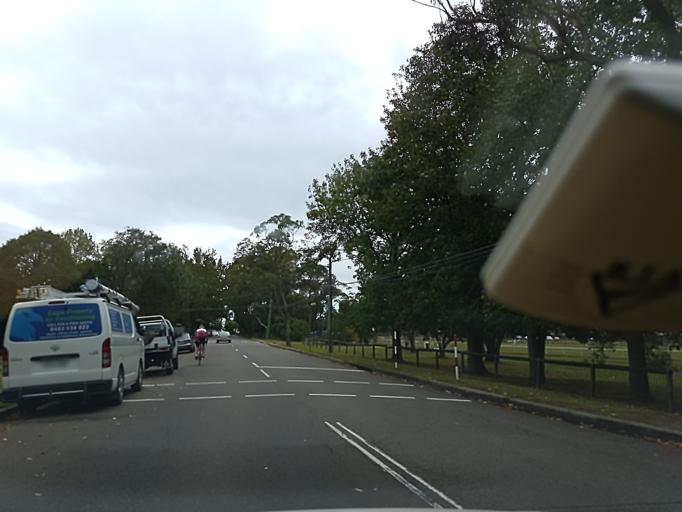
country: AU
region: New South Wales
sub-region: Warringah
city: Davidson
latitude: -33.7401
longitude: 151.2164
